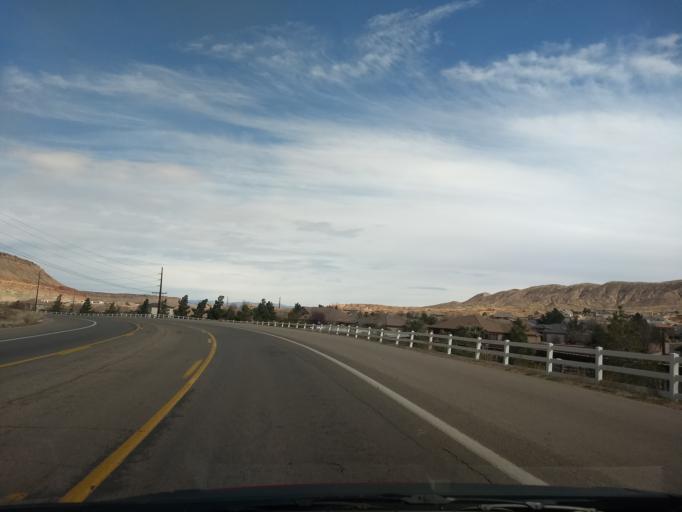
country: US
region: Utah
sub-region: Washington County
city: Washington
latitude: 37.0994
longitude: -113.4969
